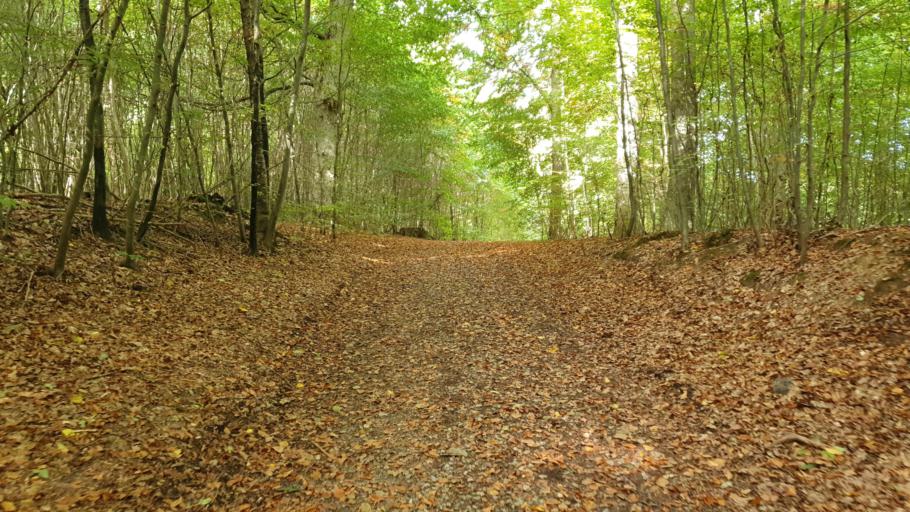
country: DE
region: North Rhine-Westphalia
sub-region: Regierungsbezirk Detmold
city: Bad Salzuflen
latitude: 52.1035
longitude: 8.7459
